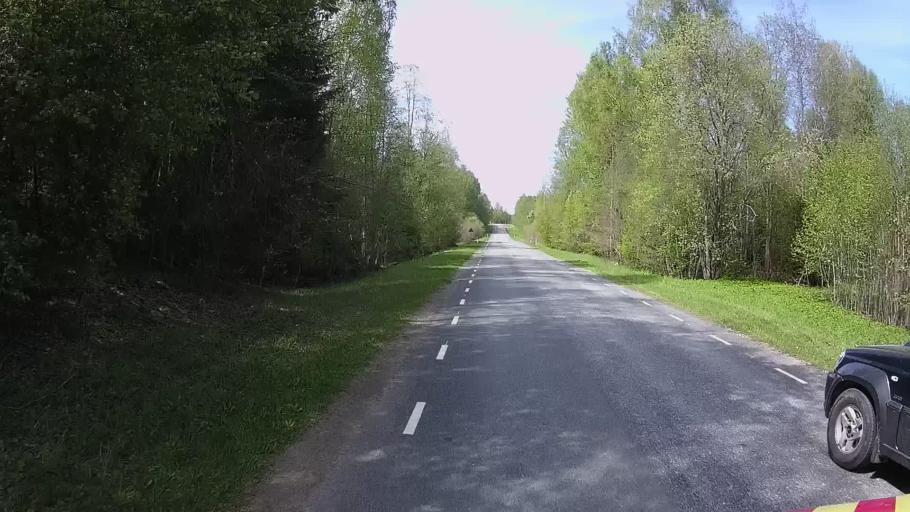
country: EE
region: Valgamaa
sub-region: Valga linn
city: Valga
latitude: 57.6545
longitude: 26.2953
